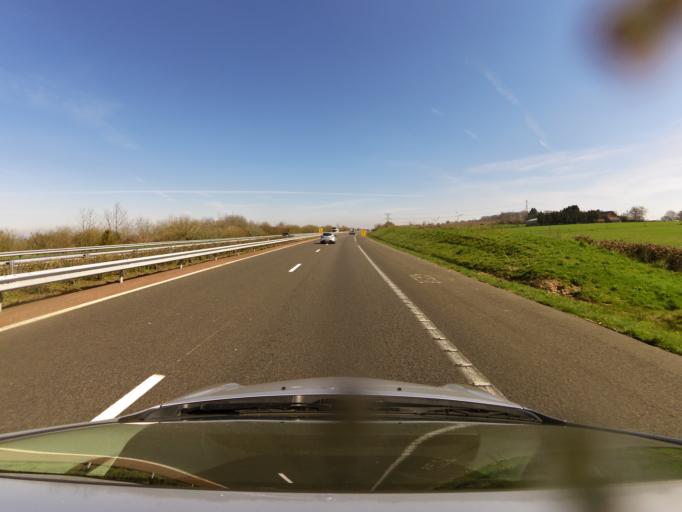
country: FR
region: Lower Normandy
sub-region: Departement de la Manche
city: Percy
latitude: 48.8851
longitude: -1.1426
